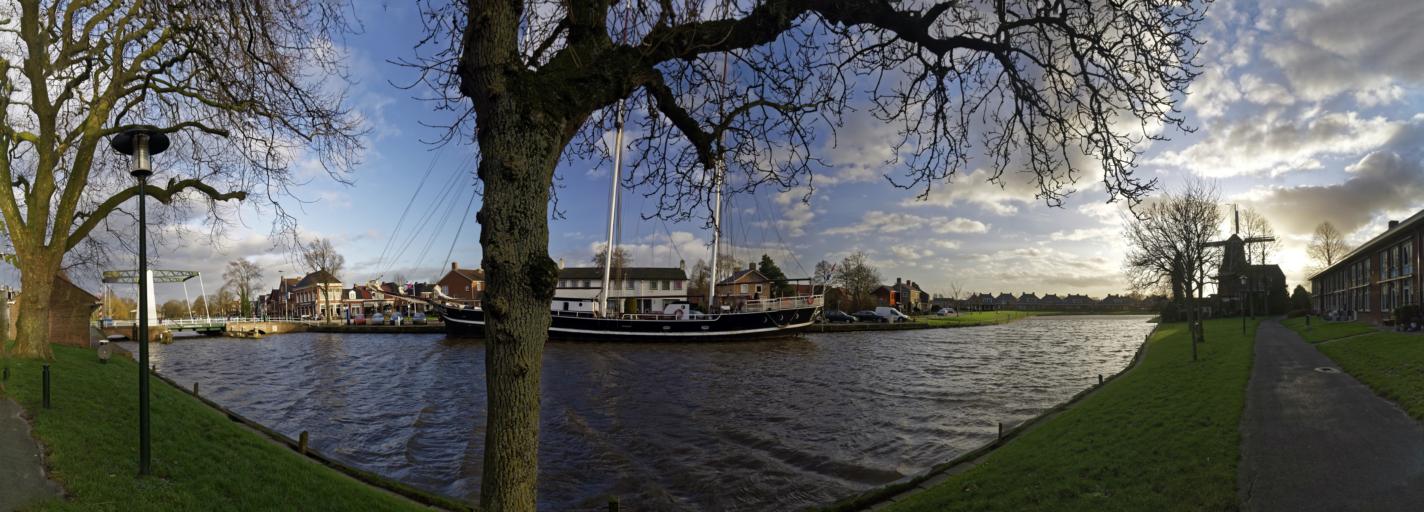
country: NL
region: Friesland
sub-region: Gemeente Dongeradeel
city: Dokkum
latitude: 53.3235
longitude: 5.9992
